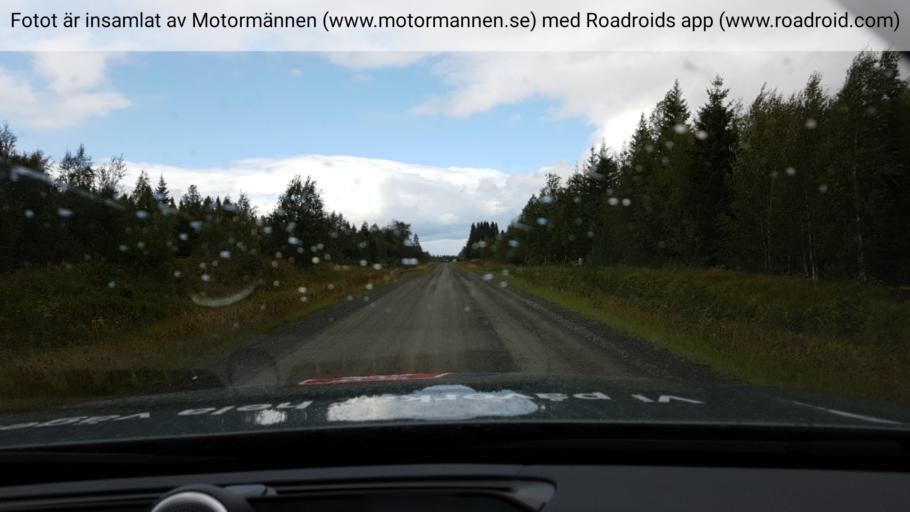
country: SE
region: Jaemtland
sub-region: OEstersunds Kommun
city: Lit
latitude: 63.6769
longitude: 14.8692
